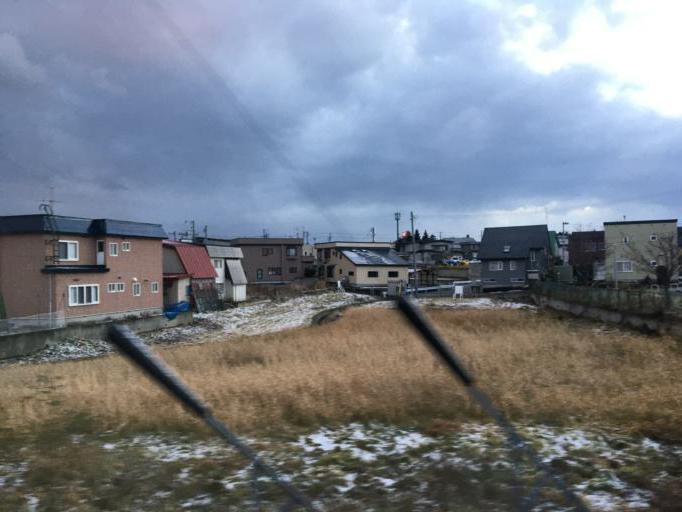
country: JP
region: Aomori
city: Aomori Shi
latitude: 40.8278
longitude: 140.6895
